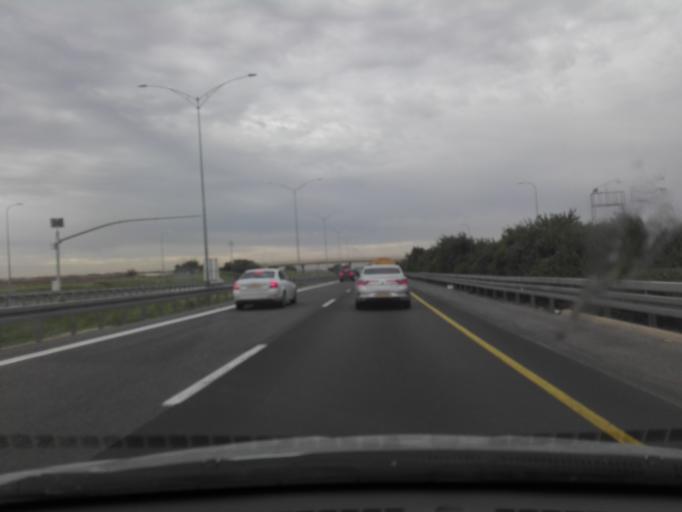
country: IL
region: Central District
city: Mazkeret Batya
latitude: 31.8817
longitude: 34.8787
